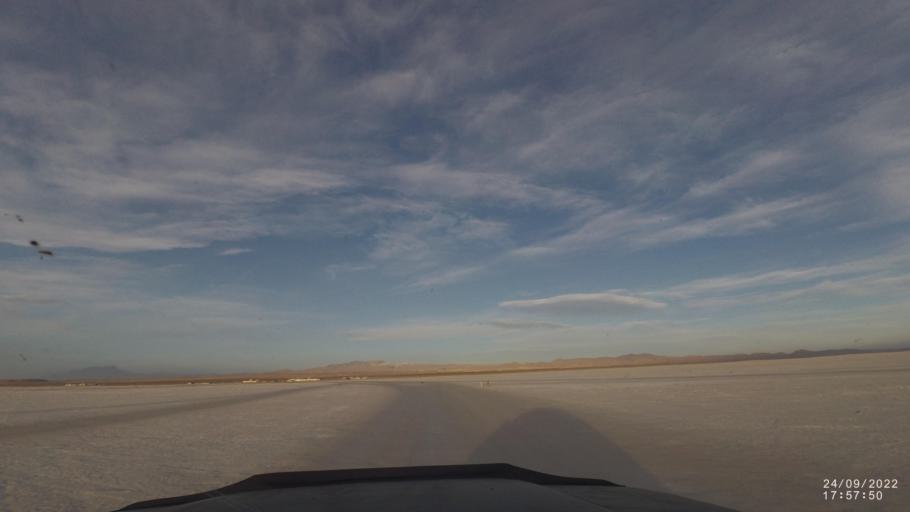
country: BO
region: Potosi
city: Colchani
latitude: -20.3185
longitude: -66.9854
